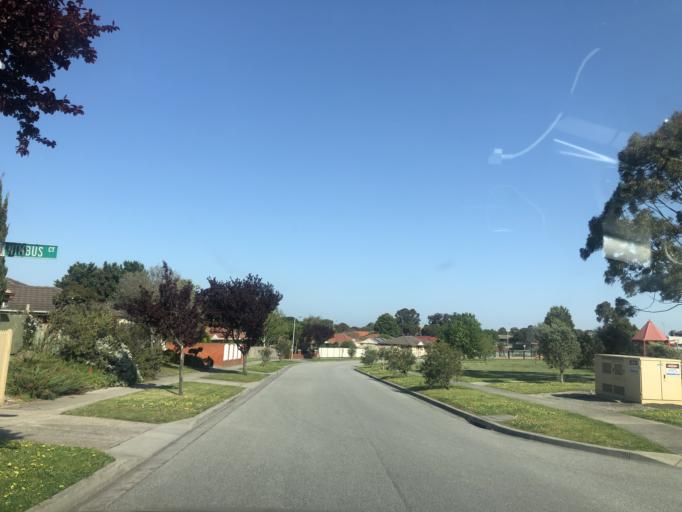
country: AU
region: Victoria
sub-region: Casey
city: Narre Warren South
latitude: -38.0470
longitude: 145.2733
